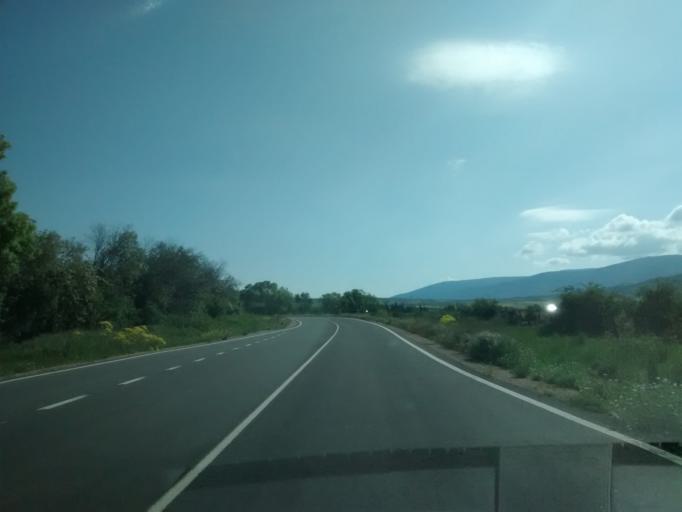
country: ES
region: Castille and Leon
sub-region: Provincia de Segovia
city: Trescasas
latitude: 40.9747
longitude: -4.0277
